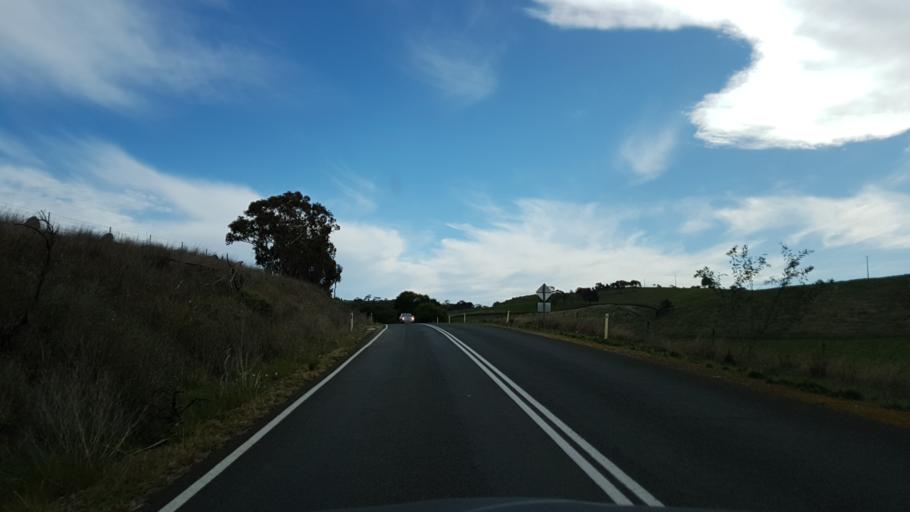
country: AU
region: South Australia
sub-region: Alexandrina
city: Strathalbyn
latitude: -35.1829
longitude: 138.9483
